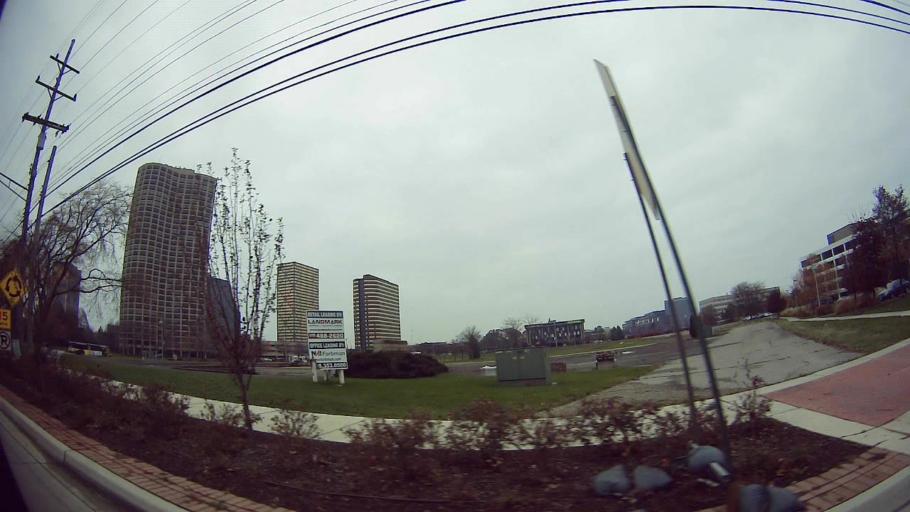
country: US
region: Michigan
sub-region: Oakland County
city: Southfield
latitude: 42.4816
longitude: -83.2410
